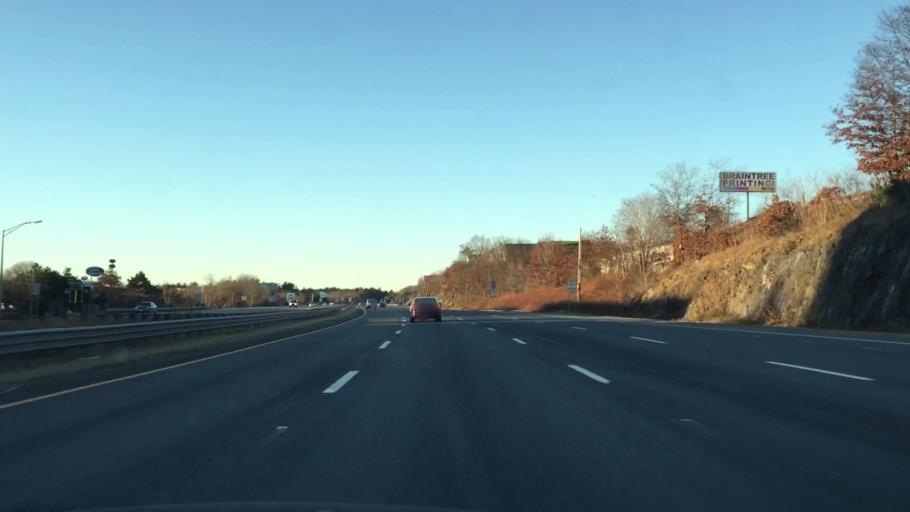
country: US
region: Massachusetts
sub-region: Norfolk County
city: Braintree
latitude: 42.2205
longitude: -71.0362
